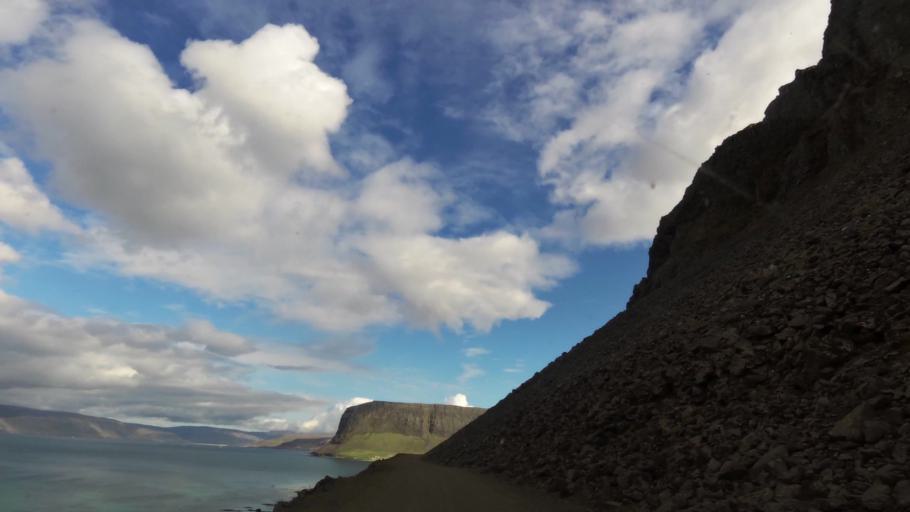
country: IS
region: West
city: Olafsvik
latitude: 65.5983
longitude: -24.1354
